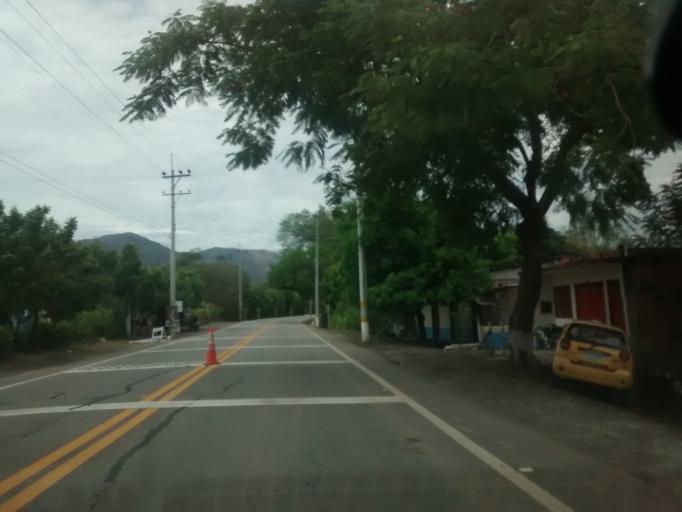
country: CO
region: Cundinamarca
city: Agua de Dios
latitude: 4.4001
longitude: -74.7339
